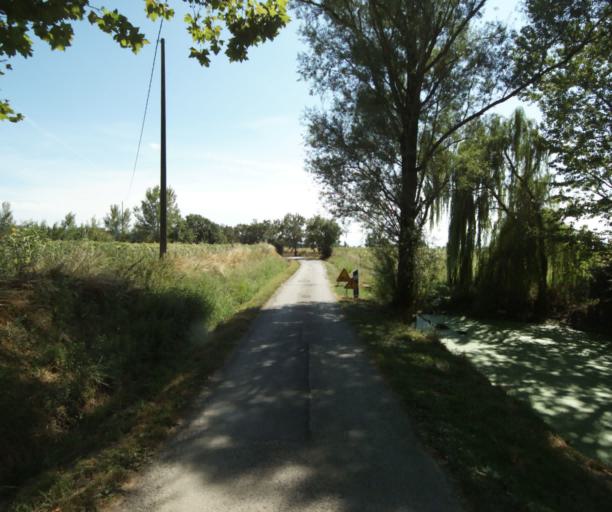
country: FR
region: Midi-Pyrenees
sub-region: Departement de la Haute-Garonne
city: Revel
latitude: 43.4993
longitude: 1.9961
